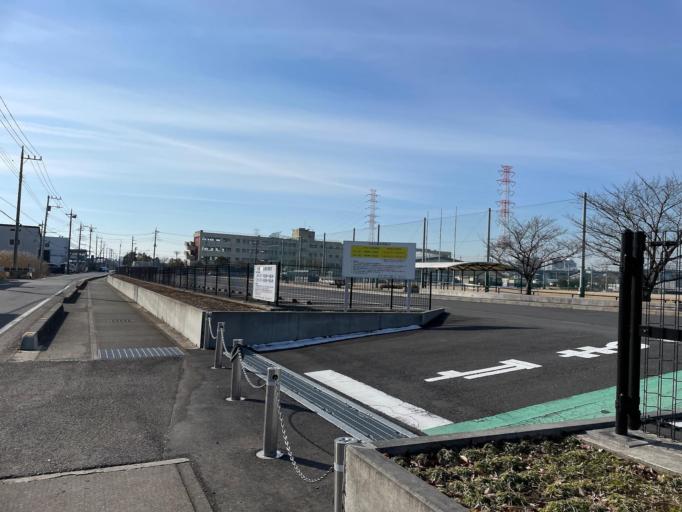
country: JP
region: Chiba
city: Nagareyama
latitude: 35.8595
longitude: 139.8761
